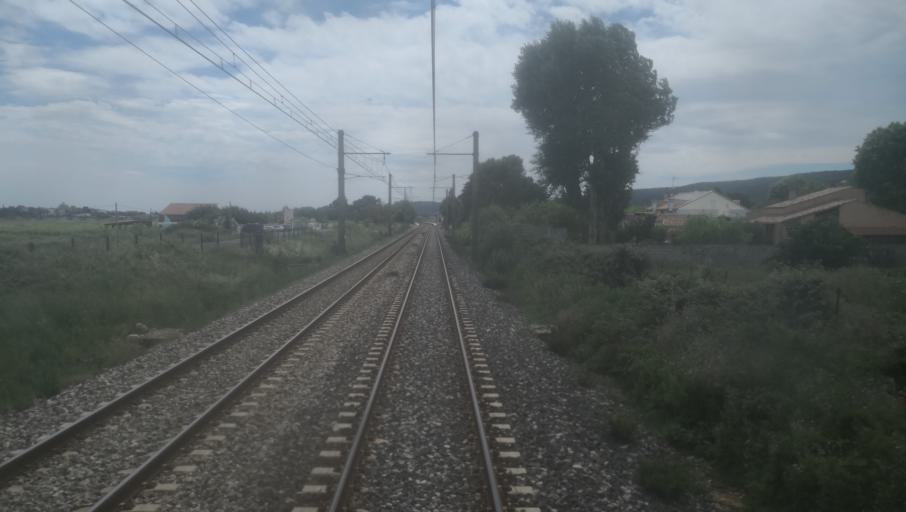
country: FR
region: Languedoc-Roussillon
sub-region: Departement de l'Herault
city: Mireval
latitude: 43.5029
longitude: 3.8023
